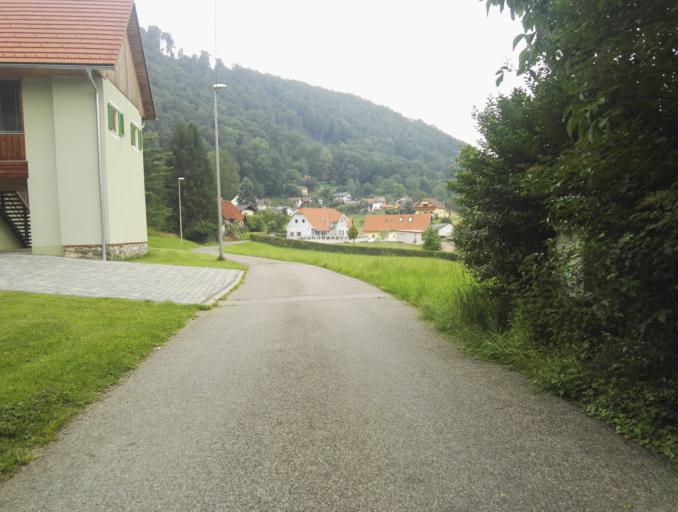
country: AT
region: Styria
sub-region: Graz Stadt
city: Goesting
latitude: 47.1105
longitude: 15.3719
